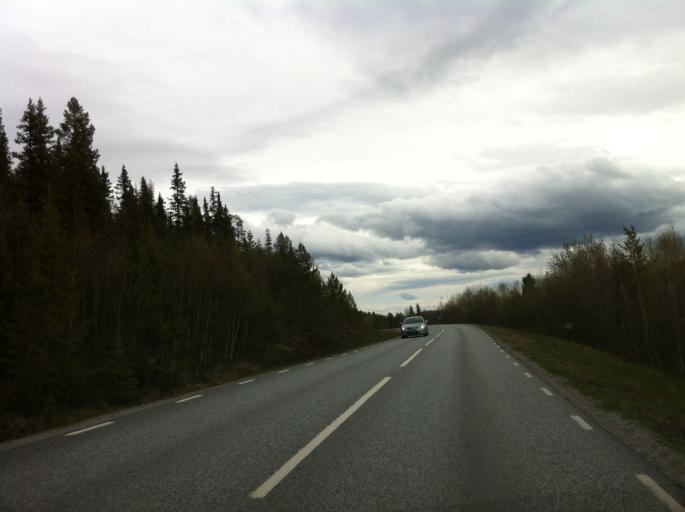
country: NO
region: Sor-Trondelag
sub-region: Tydal
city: Aas
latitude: 62.6058
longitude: 12.5066
